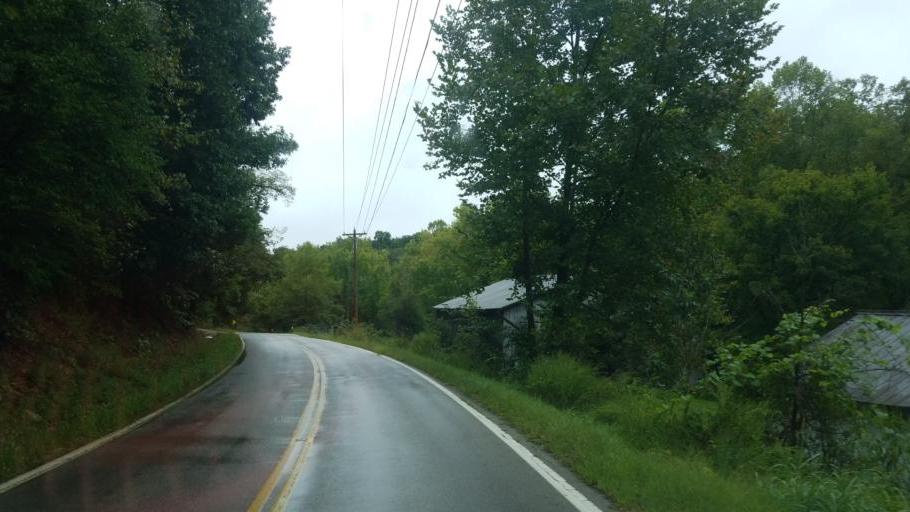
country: US
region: Ohio
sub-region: Adams County
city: West Union
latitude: 38.7695
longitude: -83.5305
